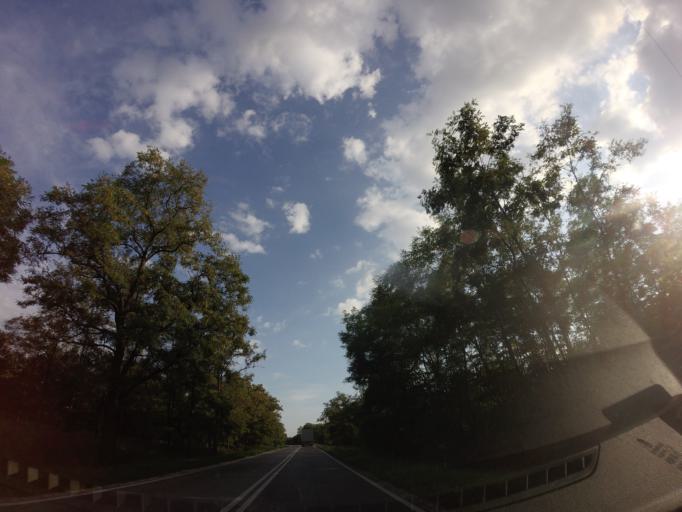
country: PL
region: Lublin Voivodeship
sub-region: Powiat lubartowski
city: Jeziorzany
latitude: 51.5848
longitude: 22.2827
